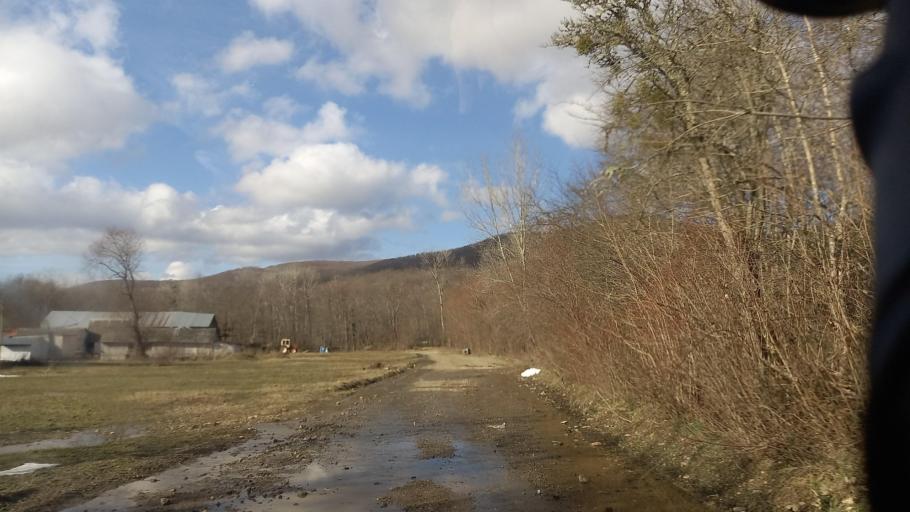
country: RU
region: Krasnodarskiy
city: Smolenskaya
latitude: 44.5982
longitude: 38.8804
